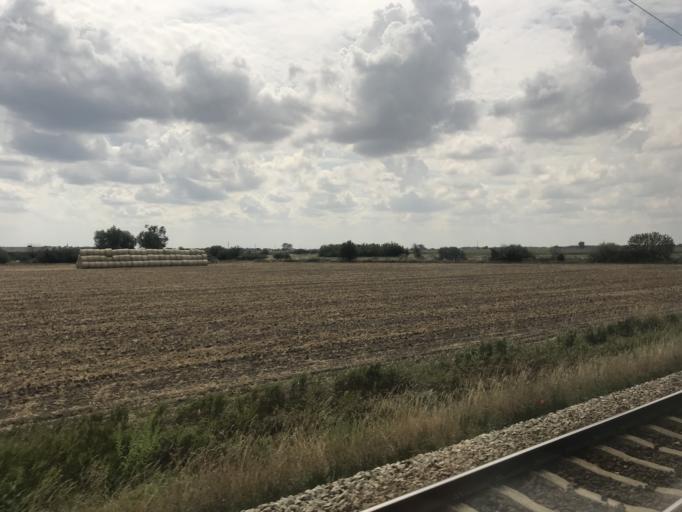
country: PL
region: Greater Poland Voivodeship
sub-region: Powiat poznanski
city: Dopiewo
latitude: 52.3620
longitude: 16.7012
